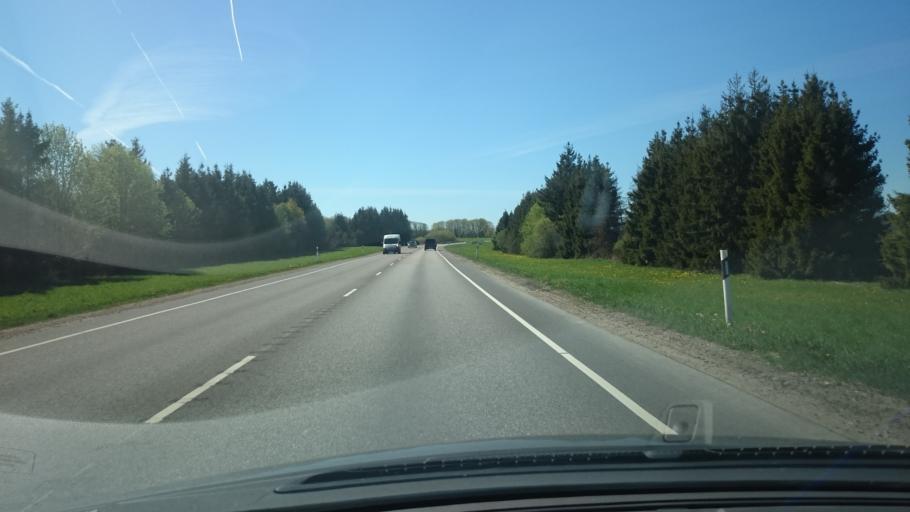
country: EE
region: Ida-Virumaa
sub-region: Sillamaee linn
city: Sillamae
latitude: 59.3768
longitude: 27.8925
